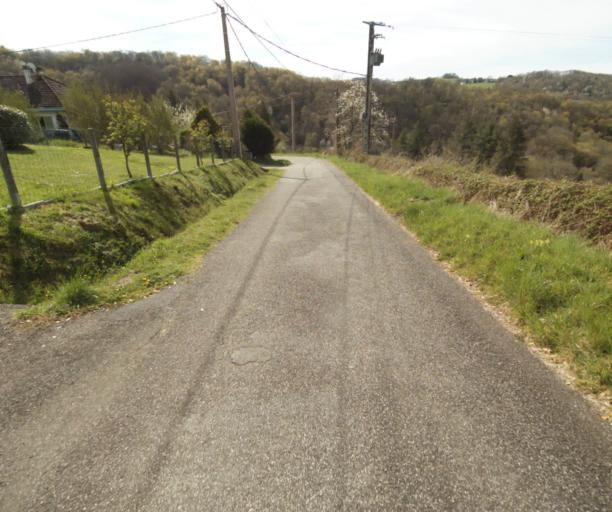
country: FR
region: Limousin
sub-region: Departement de la Correze
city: Laguenne
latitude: 45.2510
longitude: 1.8207
